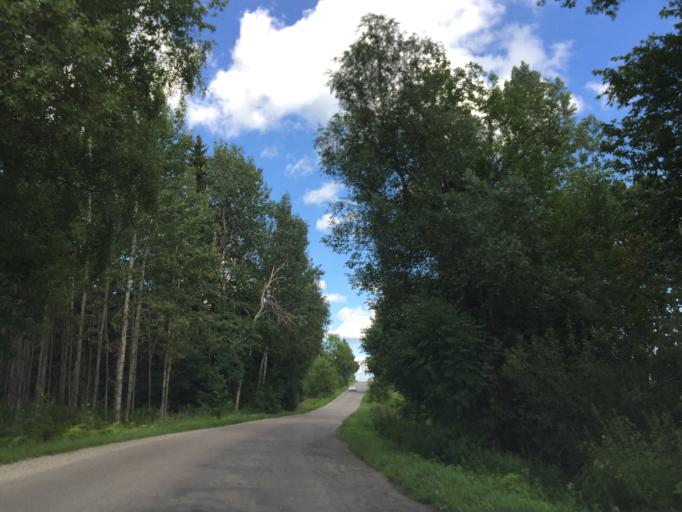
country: PL
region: Podlasie
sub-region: Suwalki
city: Suwalki
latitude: 54.1240
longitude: 23.0174
